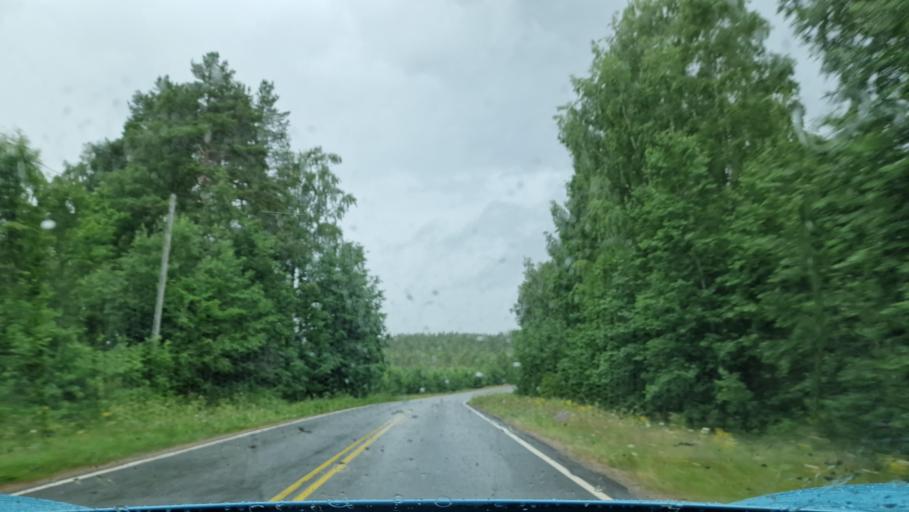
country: FI
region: Southern Ostrobothnia
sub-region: Jaerviseutu
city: Soini
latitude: 62.8049
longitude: 24.3643
